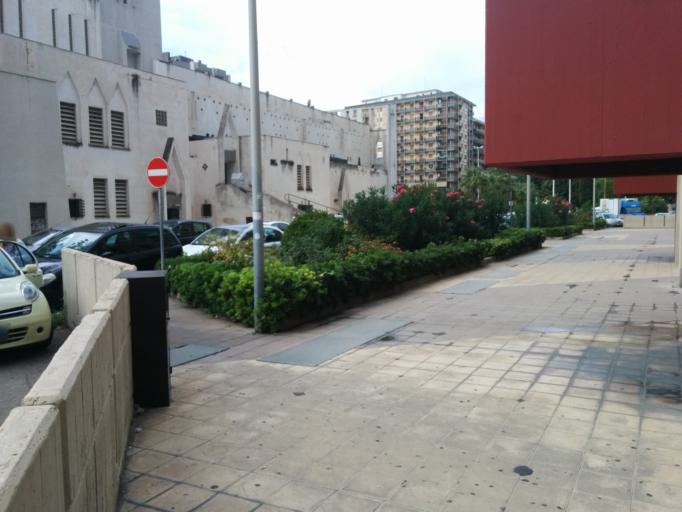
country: IT
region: Apulia
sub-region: Provincia di Taranto
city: Taranto
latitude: 40.4622
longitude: 17.2711
